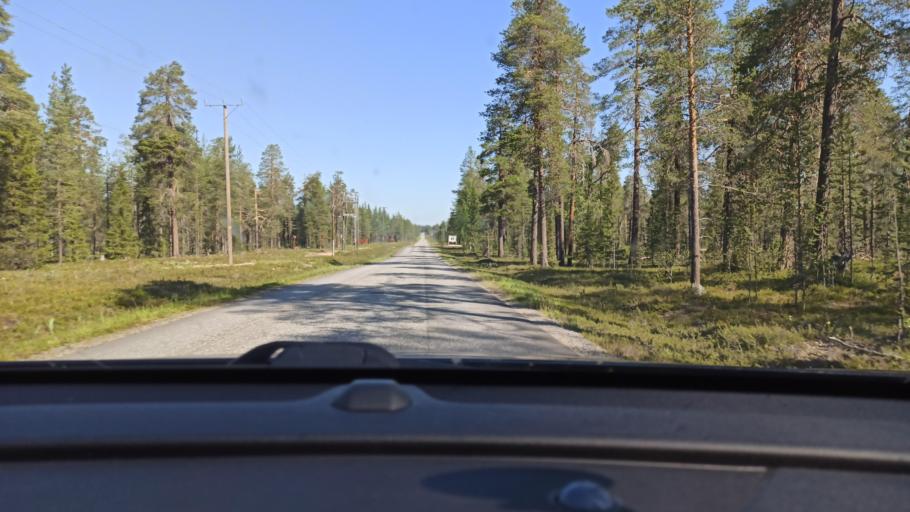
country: FI
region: Lapland
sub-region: Tunturi-Lappi
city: Kolari
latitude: 67.6441
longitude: 24.1593
